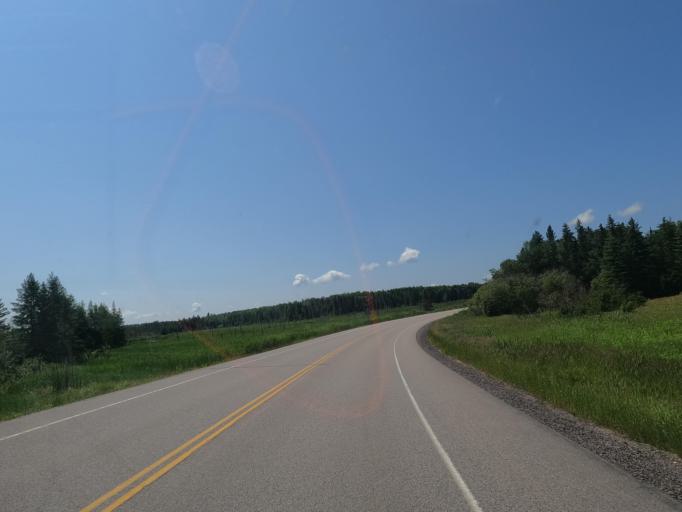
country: CA
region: Ontario
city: Dryden
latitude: 49.9050
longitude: -93.3596
